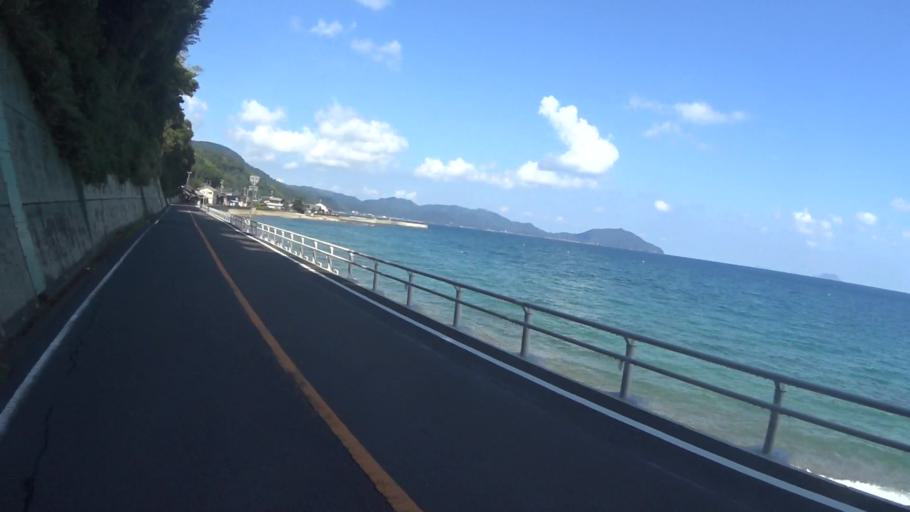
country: JP
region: Kyoto
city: Miyazu
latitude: 35.6217
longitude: 135.2449
